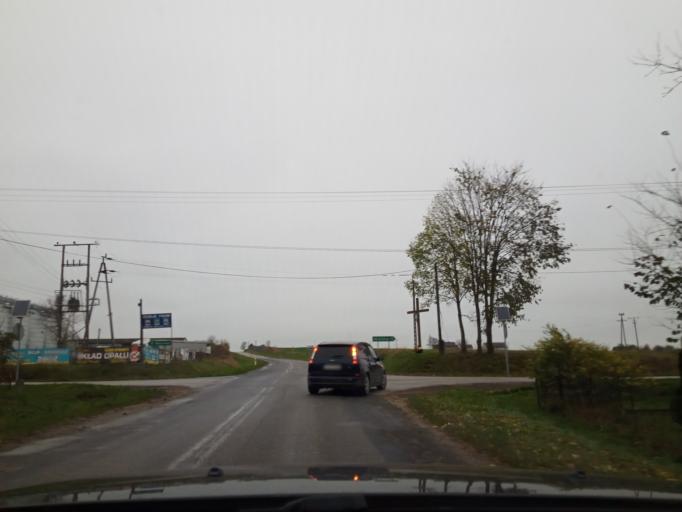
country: PL
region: Swietokrzyskie
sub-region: Powiat jedrzejowski
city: Jedrzejow
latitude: 50.5192
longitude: 20.3242
